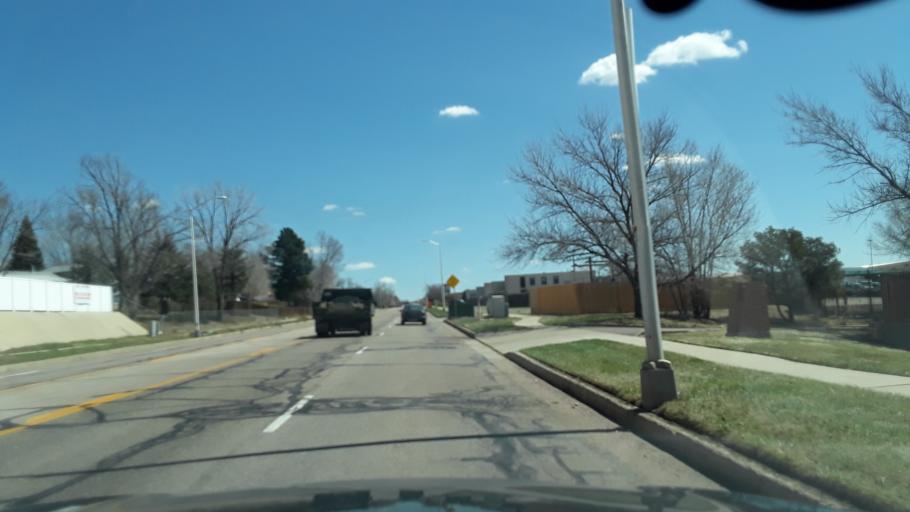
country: US
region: Colorado
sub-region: El Paso County
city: Cimarron Hills
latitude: 38.8468
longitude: -104.7339
